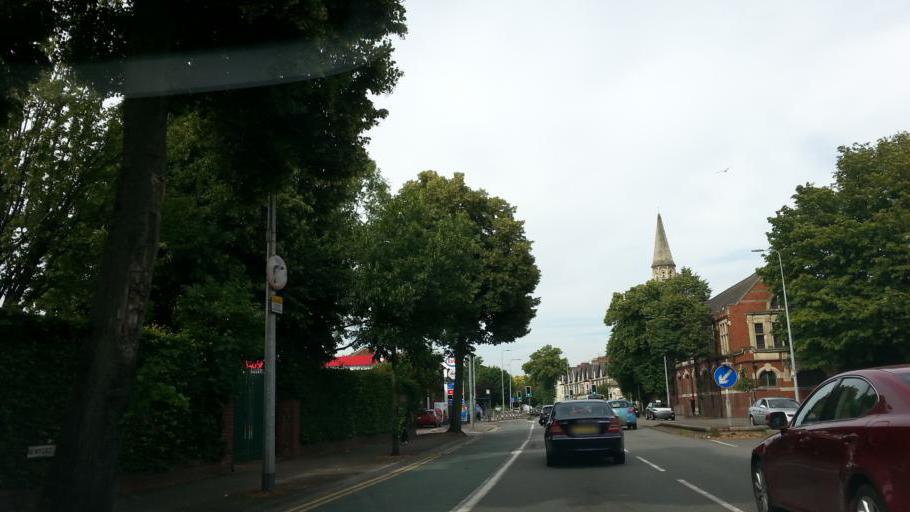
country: GB
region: Wales
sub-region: Cardiff
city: Cardiff
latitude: 51.4866
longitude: -3.1609
